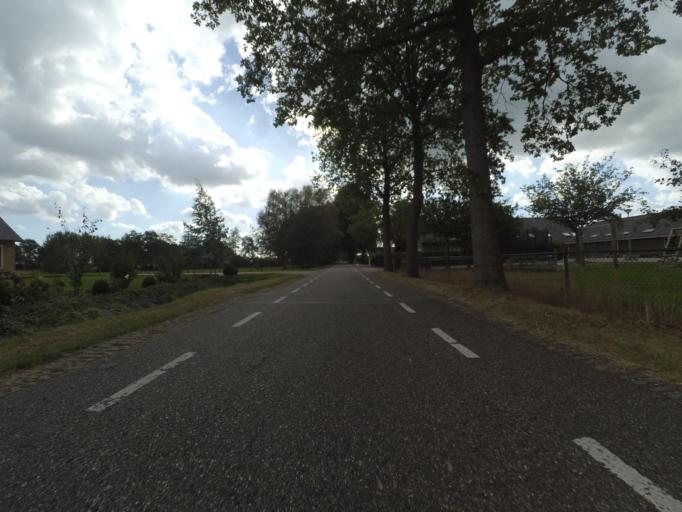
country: NL
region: Utrecht
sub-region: Gemeente Utrechtse Heuvelrug
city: Overberg
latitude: 52.0623
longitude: 5.5209
